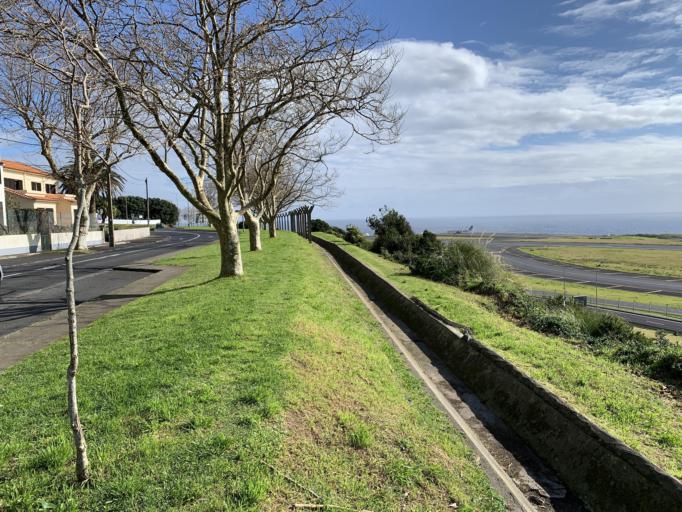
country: PT
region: Azores
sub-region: Ponta Delgada
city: Arrifes
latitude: 37.7480
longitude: -25.7056
